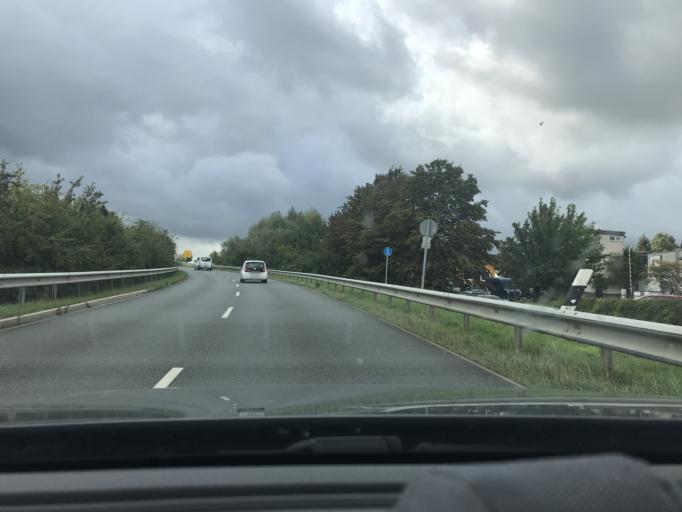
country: DE
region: North Rhine-Westphalia
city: Haan
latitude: 51.2131
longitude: 7.0177
